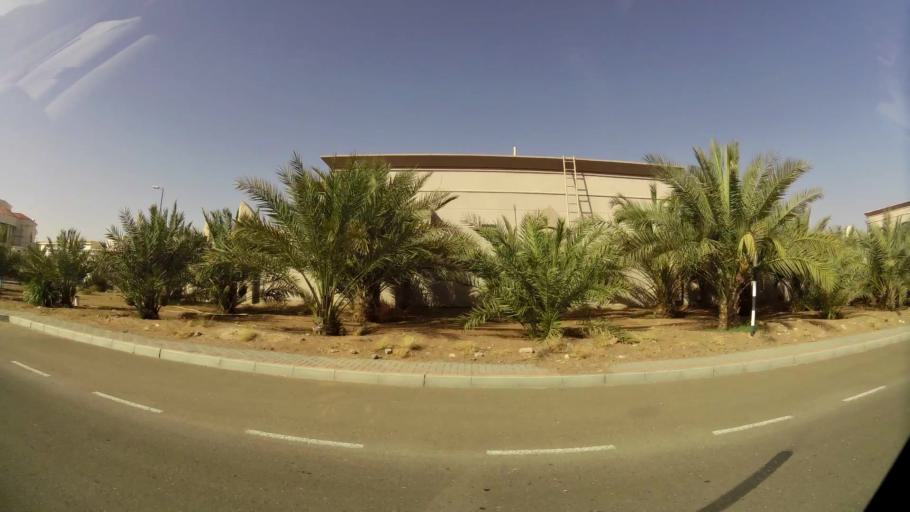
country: OM
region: Al Buraimi
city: Al Buraymi
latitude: 24.3472
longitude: 55.7951
